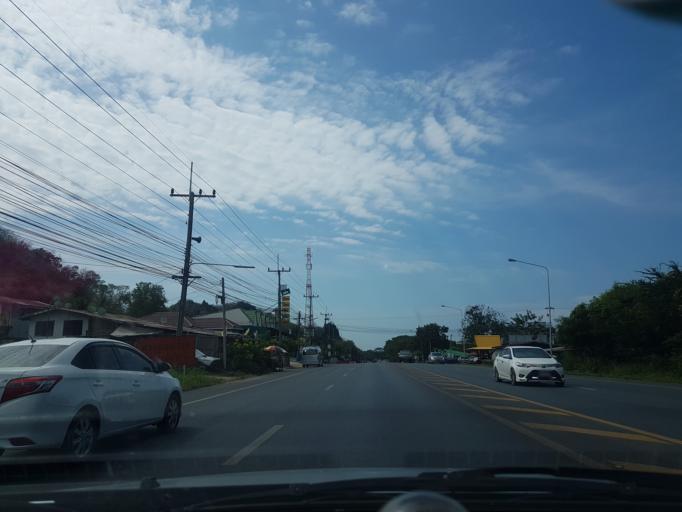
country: TH
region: Sara Buri
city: Phra Phutthabat
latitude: 14.8058
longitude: 100.7669
